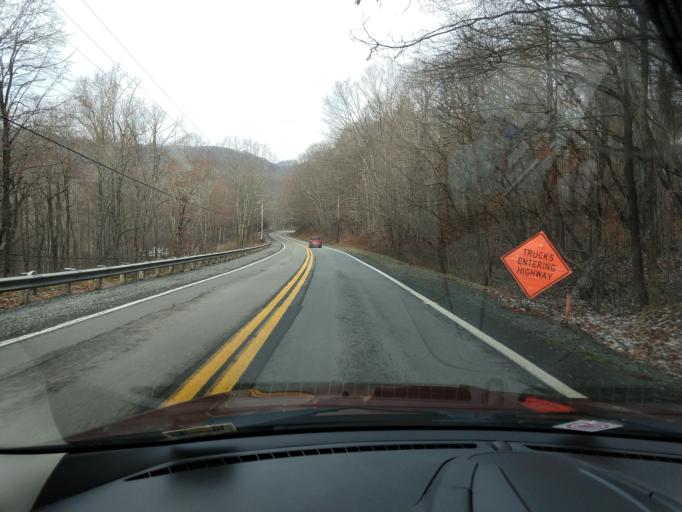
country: US
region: West Virginia
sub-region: Greenbrier County
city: Rainelle
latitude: 38.0323
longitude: -80.7283
